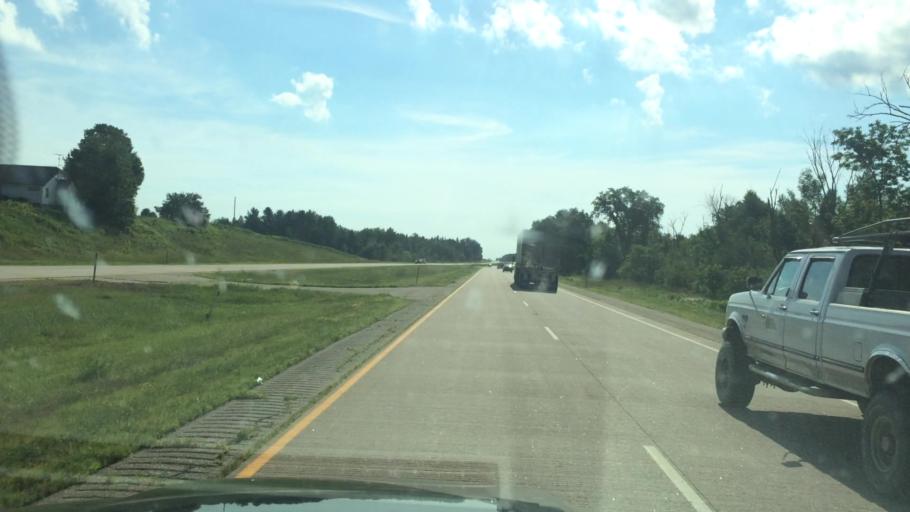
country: US
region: Wisconsin
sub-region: Waupaca County
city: Marion
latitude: 44.8041
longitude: -88.9655
